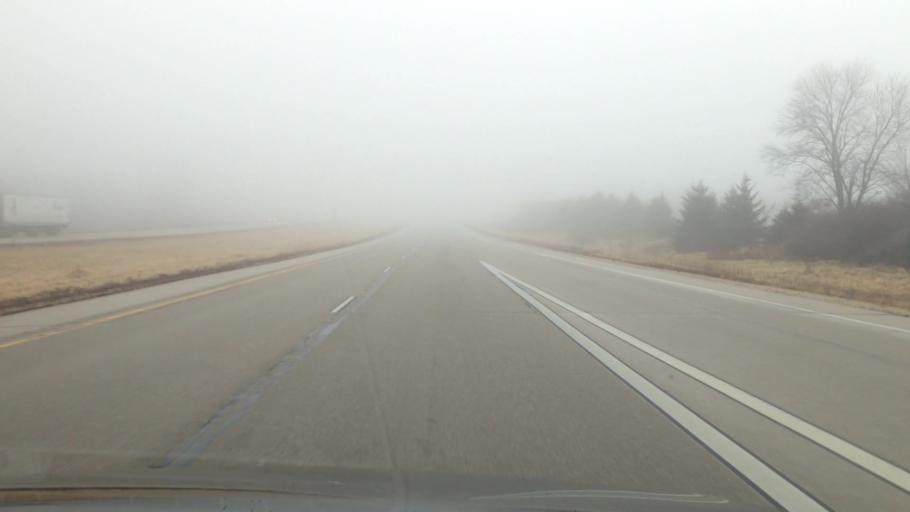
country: US
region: Wisconsin
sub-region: Walworth County
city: Elkhorn
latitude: 42.6955
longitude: -88.4986
